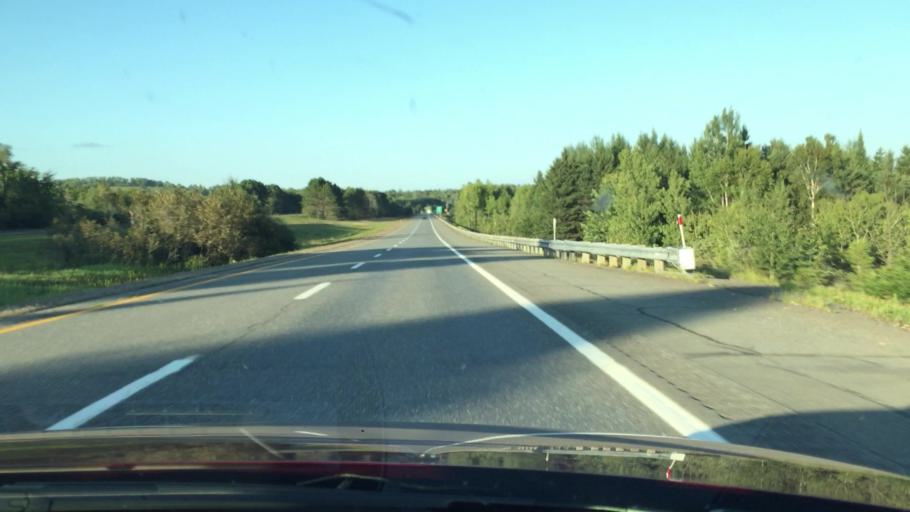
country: US
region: Maine
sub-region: Aroostook County
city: Hodgdon
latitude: 46.1398
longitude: -68.0717
